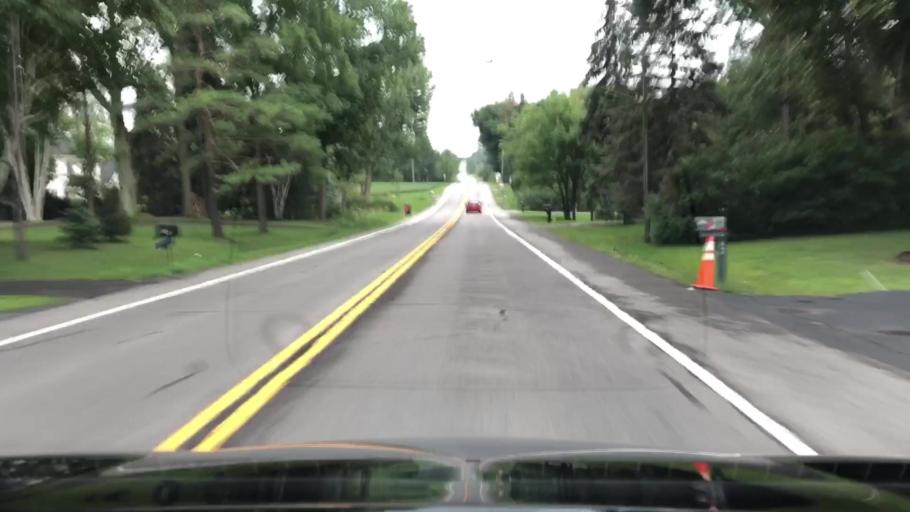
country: US
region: New York
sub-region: Erie County
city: Orchard Park
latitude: 42.7833
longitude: -78.6969
